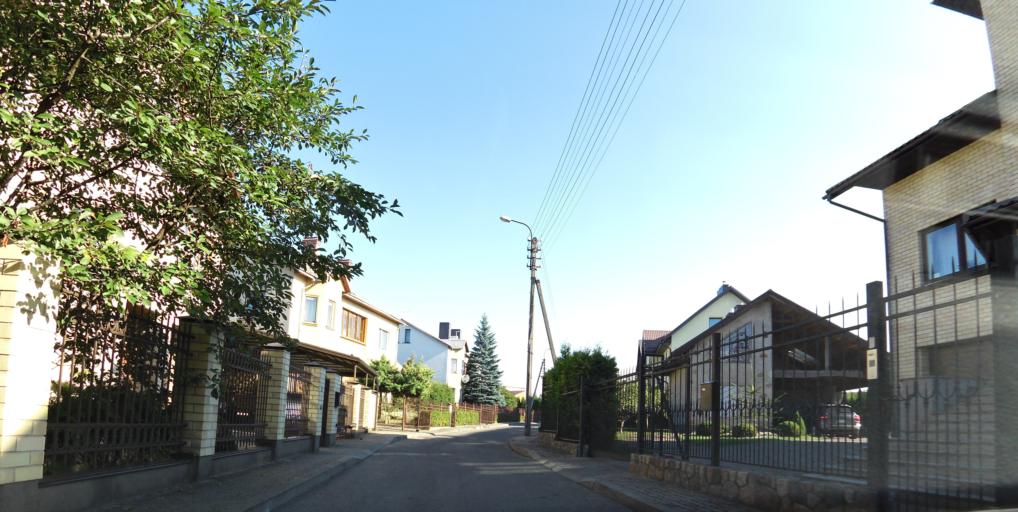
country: LT
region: Vilnius County
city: Pilaite
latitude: 54.7126
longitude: 25.1930
